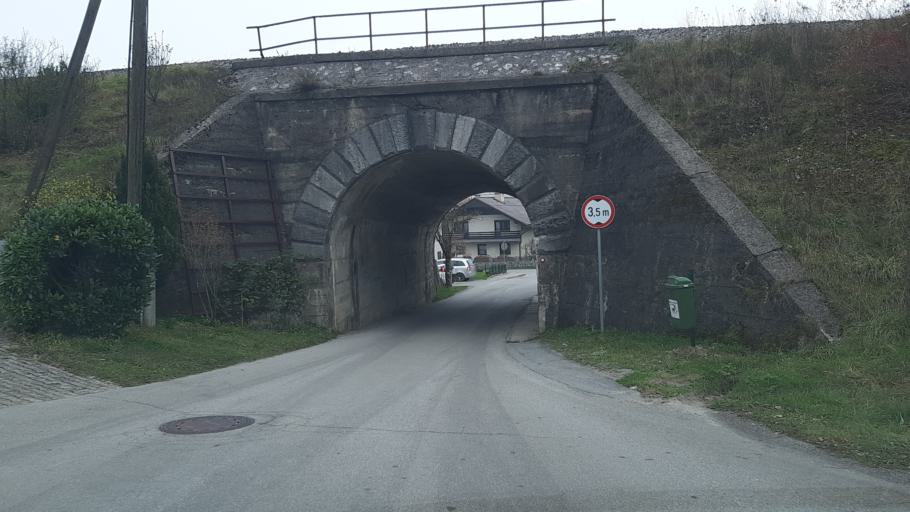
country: SI
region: Borovnica
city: Borovnica
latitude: 45.9139
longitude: 14.3643
